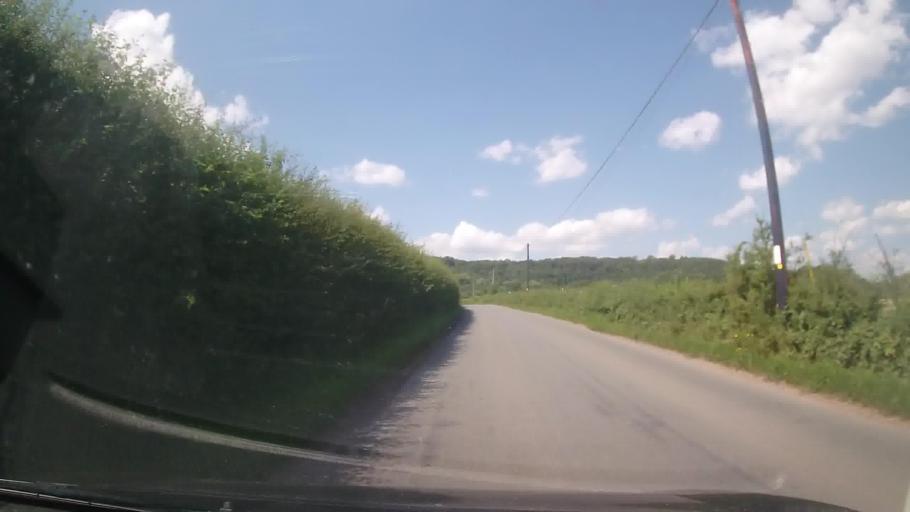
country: GB
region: England
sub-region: Herefordshire
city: Ocle Pychard
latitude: 52.0773
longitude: -2.5887
